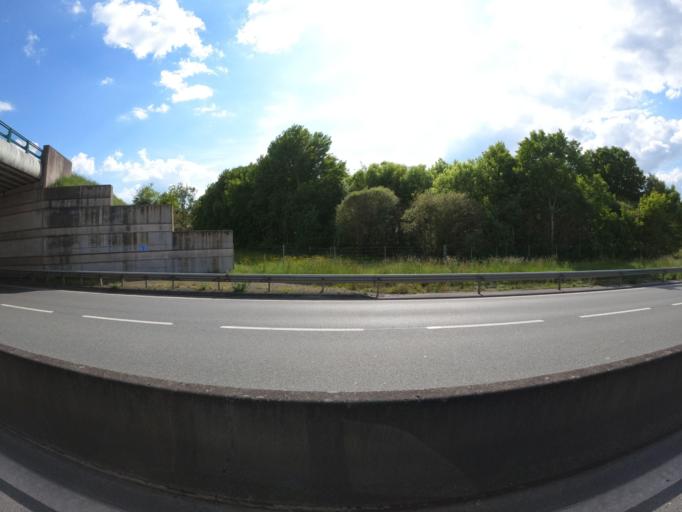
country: FR
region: Pays de la Loire
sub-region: Departement de Maine-et-Loire
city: La Tessoualle
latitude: 47.0213
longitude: -0.8833
